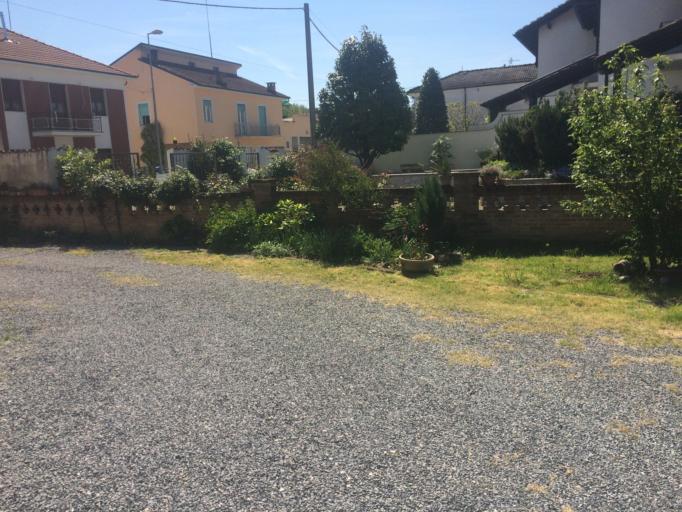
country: IT
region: Piedmont
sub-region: Provincia di Asti
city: Castagnole delle Lanze
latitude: 44.7449
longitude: 8.1524
